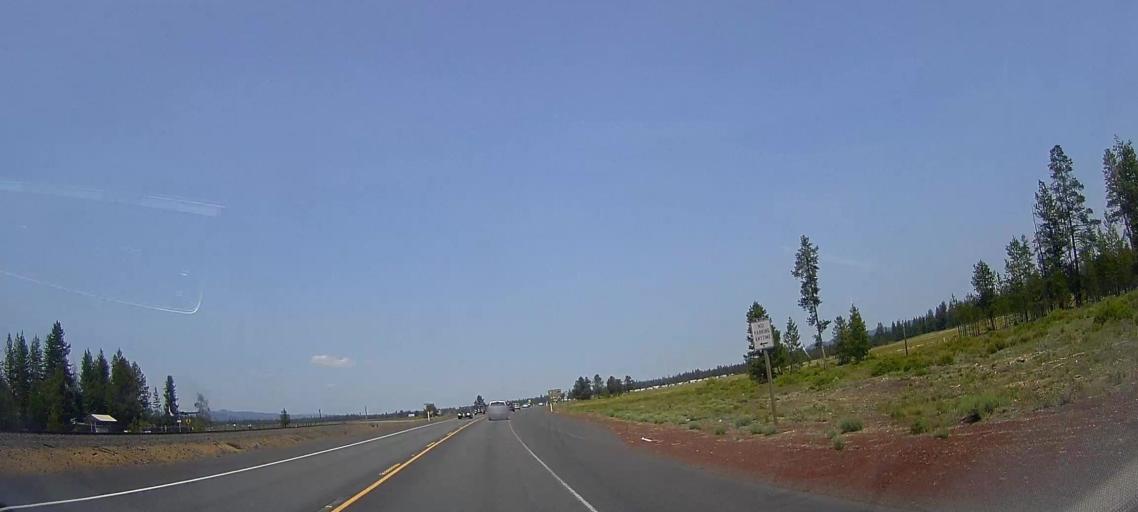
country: US
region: Oregon
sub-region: Deschutes County
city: La Pine
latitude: 43.7381
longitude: -121.4677
